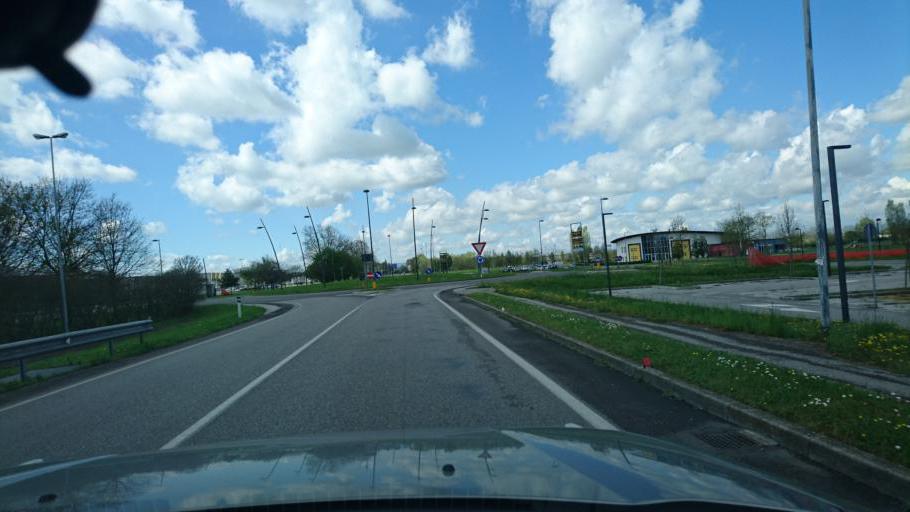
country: IT
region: Veneto
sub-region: Provincia di Padova
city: Piazzola sul Brenta
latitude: 45.5277
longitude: 11.7910
